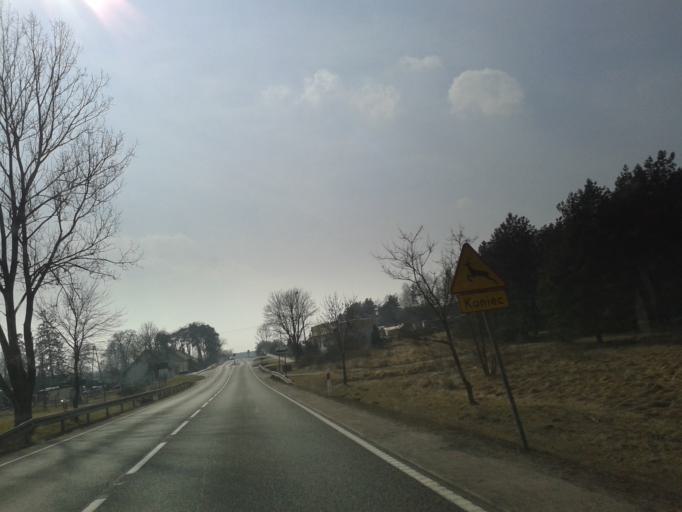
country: PL
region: Pomeranian Voivodeship
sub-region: Powiat czluchowski
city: Debrzno
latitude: 53.5852
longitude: 17.1154
